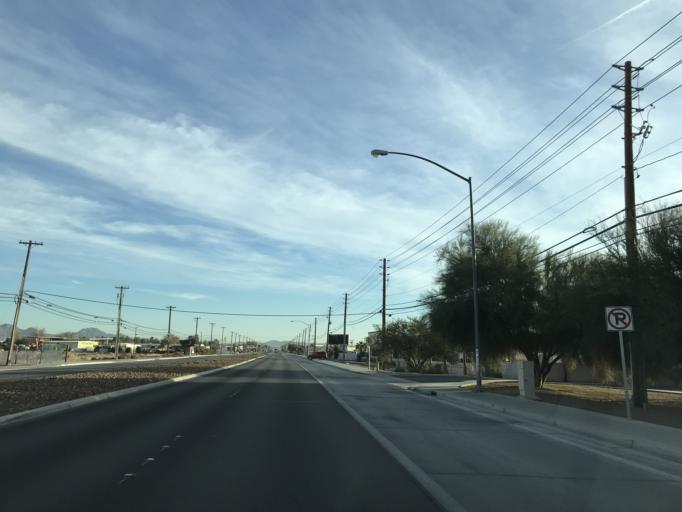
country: US
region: Nevada
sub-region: Clark County
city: Nellis Air Force Base
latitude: 36.2321
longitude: -115.0686
